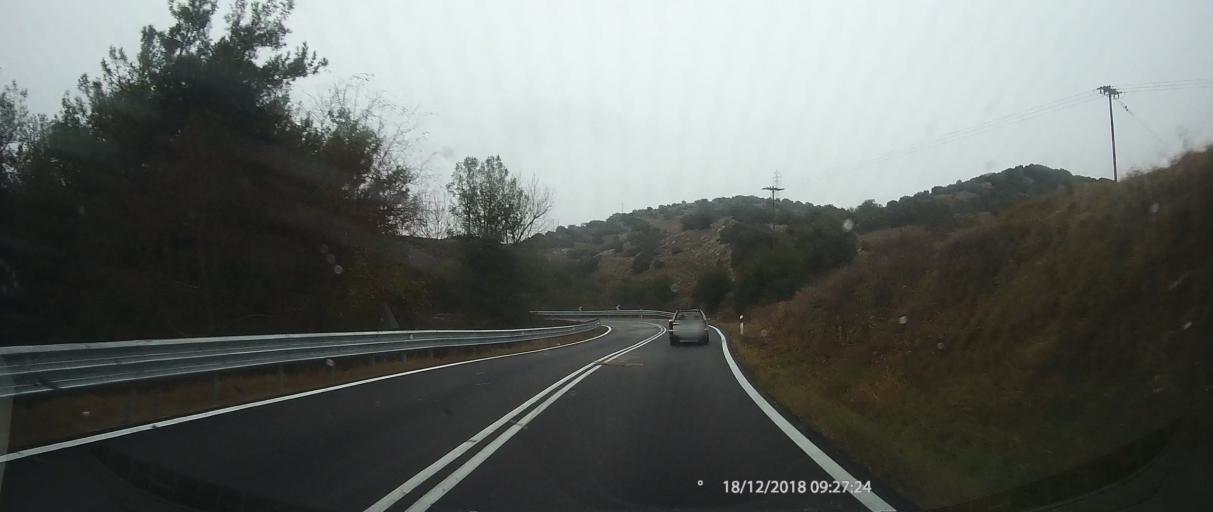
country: GR
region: Thessaly
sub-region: Nomos Larisis
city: Elassona
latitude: 39.9178
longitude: 22.1773
